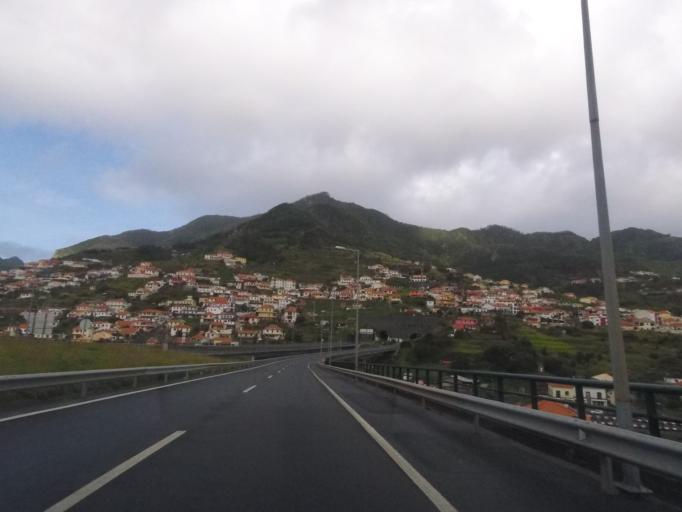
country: PT
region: Madeira
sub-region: Machico
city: Machico
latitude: 32.7308
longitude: -16.7786
